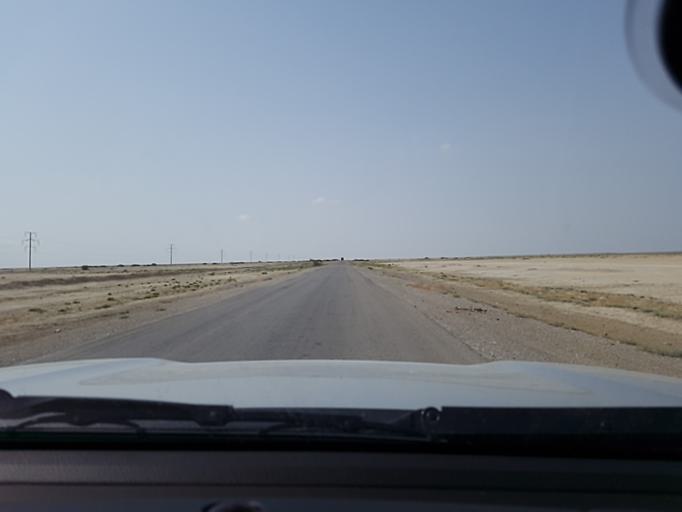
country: TM
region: Balkan
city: Gumdag
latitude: 38.9417
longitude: 54.5898
